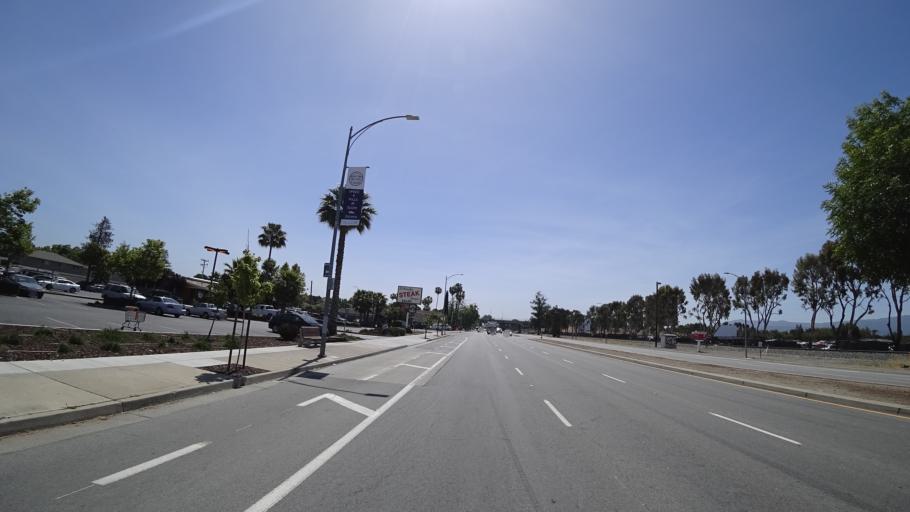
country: US
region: California
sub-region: Santa Clara County
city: Seven Trees
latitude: 37.2823
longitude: -121.8395
